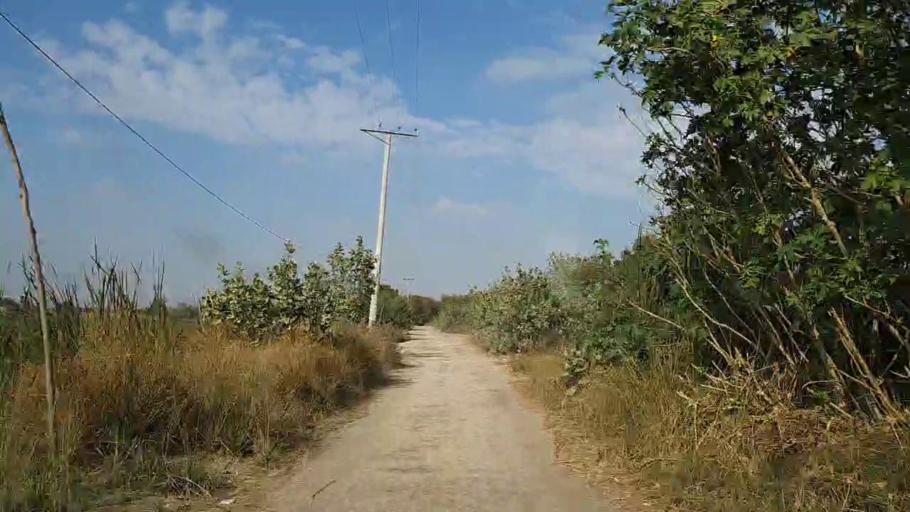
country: PK
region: Sindh
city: Sanghar
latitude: 26.2767
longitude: 69.0092
